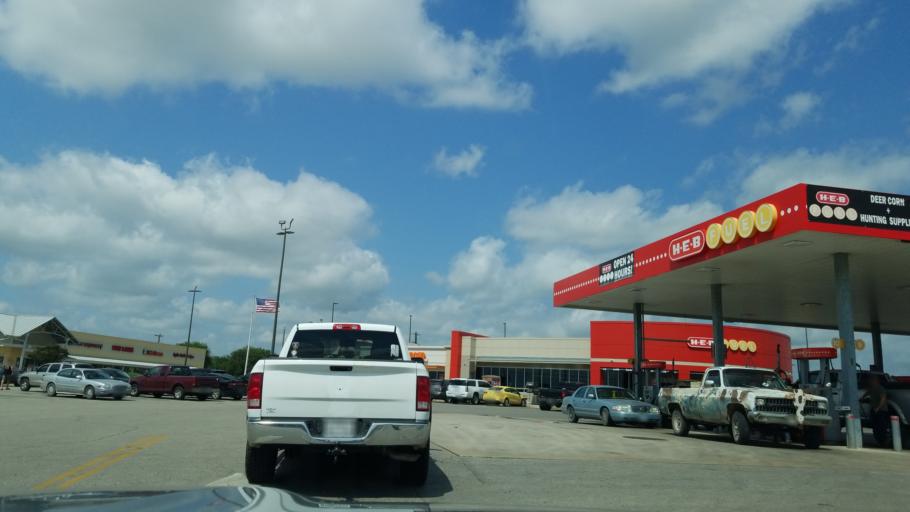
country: US
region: Texas
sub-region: Atascosa County
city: Lytle
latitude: 29.2306
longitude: -98.7887
